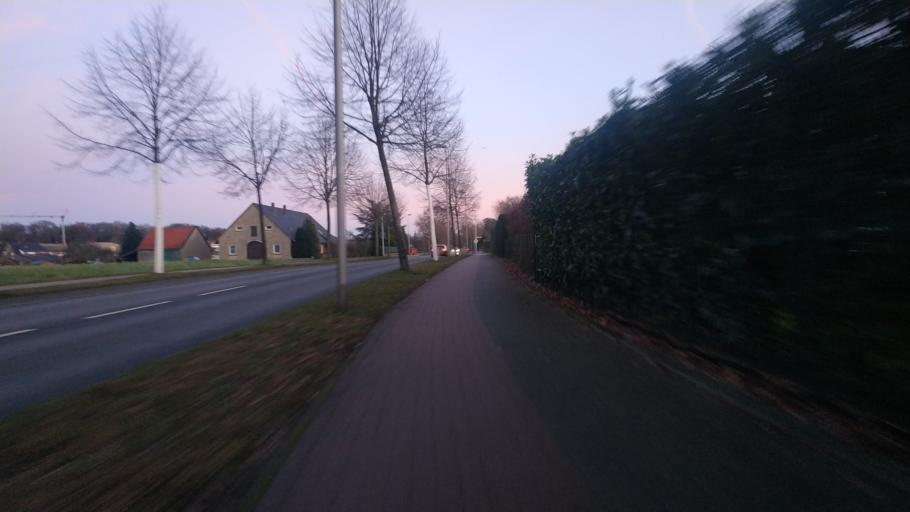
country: DE
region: North Rhine-Westphalia
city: Ibbenburen
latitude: 52.2737
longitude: 7.6841
